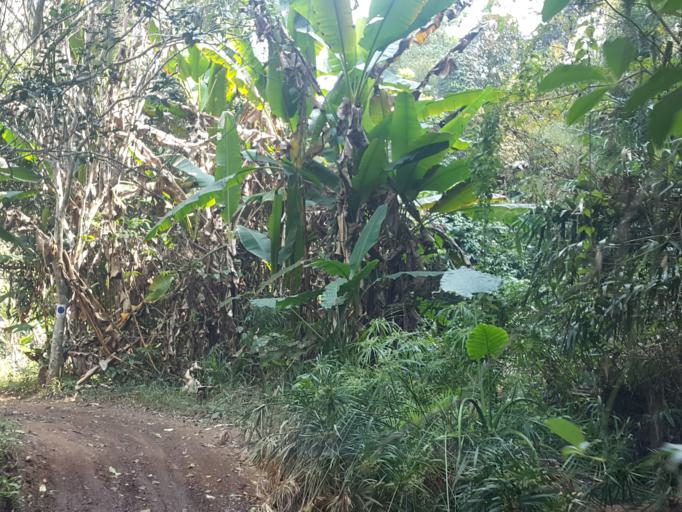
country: TH
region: Chiang Mai
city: Hang Dong
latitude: 18.7587
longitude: 98.8204
